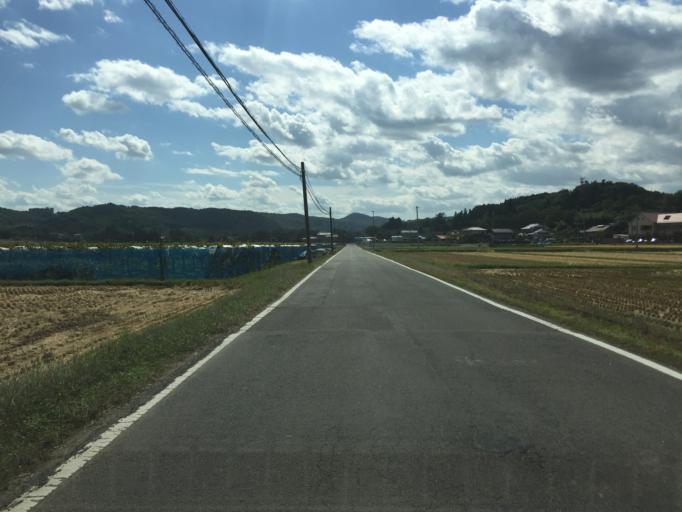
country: JP
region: Fukushima
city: Fukushima-shi
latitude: 37.7157
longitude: 140.4486
